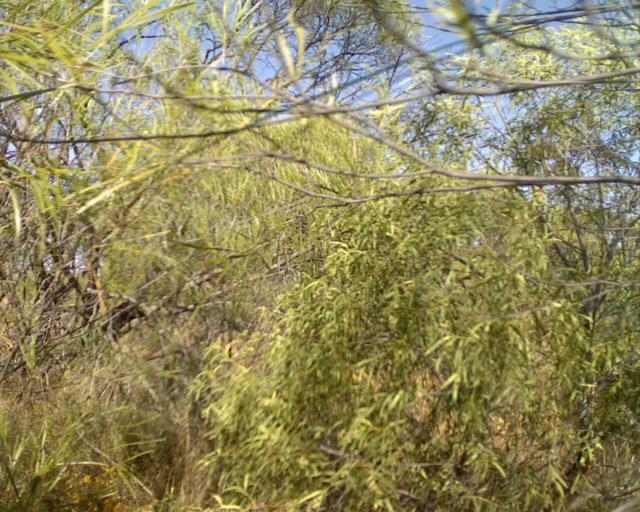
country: AU
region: Western Australia
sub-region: Moora
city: Moora
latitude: -30.1505
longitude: 116.4741
